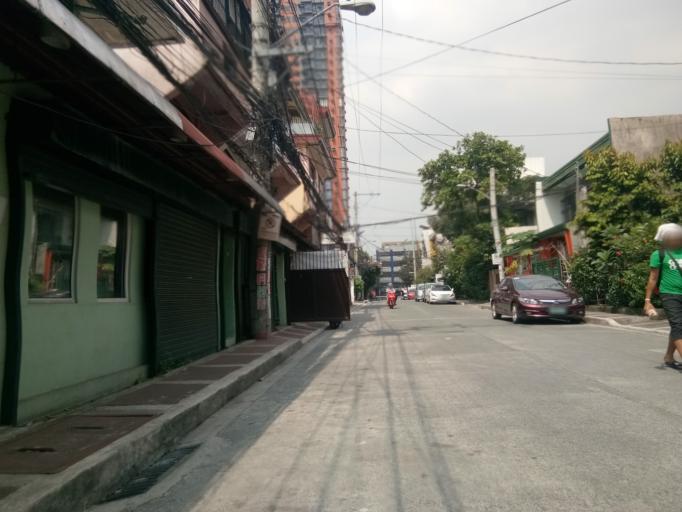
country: PH
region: Metro Manila
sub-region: Marikina
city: Calumpang
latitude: 14.6183
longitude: 121.0594
